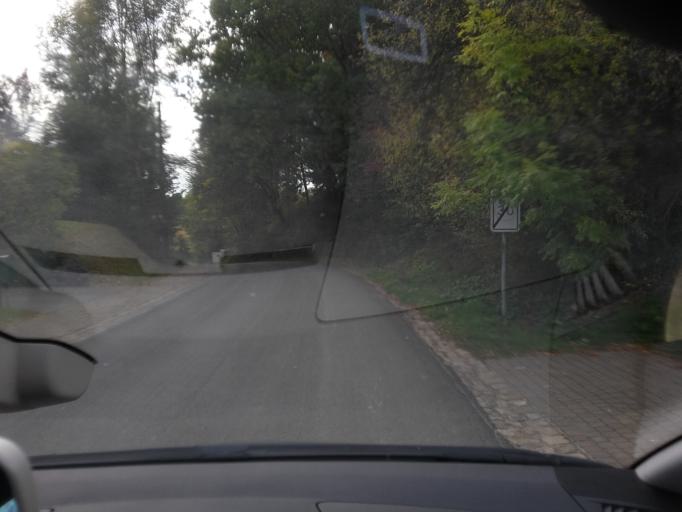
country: BE
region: Wallonia
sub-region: Province du Luxembourg
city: Attert
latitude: 49.7225
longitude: 5.7935
